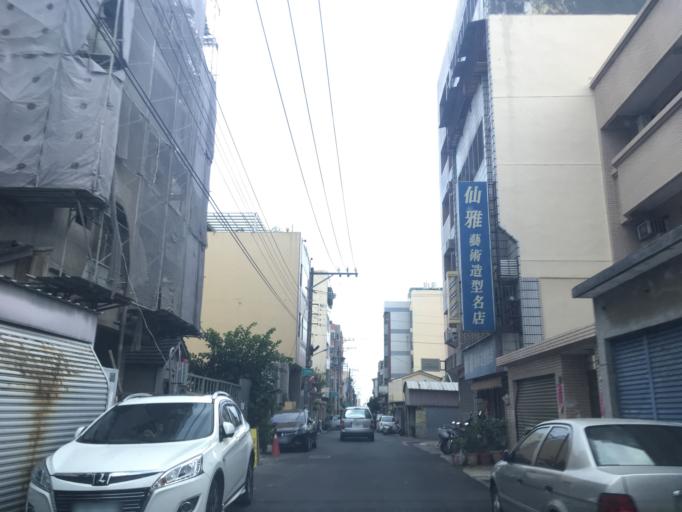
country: TW
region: Taiwan
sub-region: Taichung City
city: Taichung
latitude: 24.1687
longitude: 120.7020
